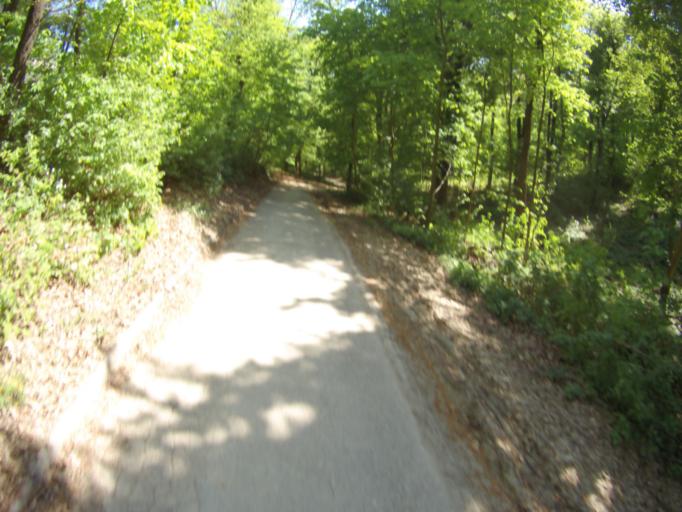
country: HU
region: Pest
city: Budaors
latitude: 47.4842
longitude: 18.9671
